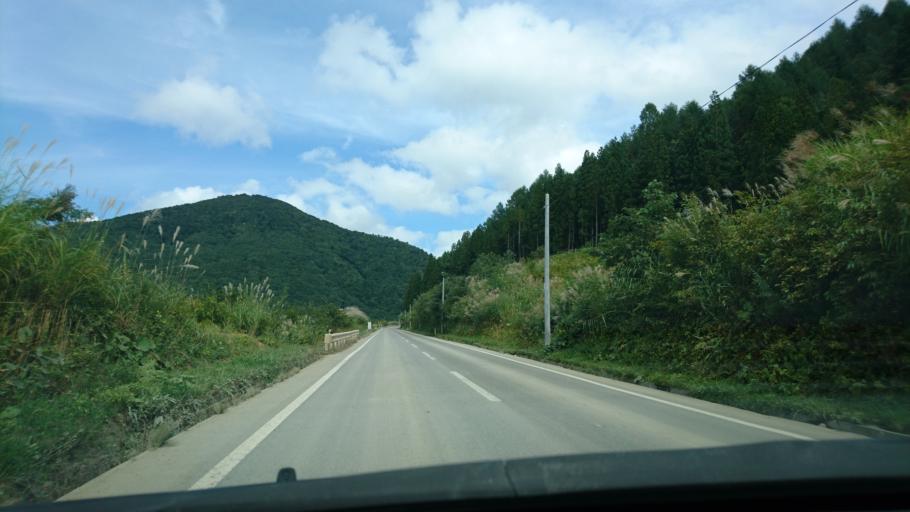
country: JP
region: Akita
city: Yuzawa
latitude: 39.0315
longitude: 140.7283
